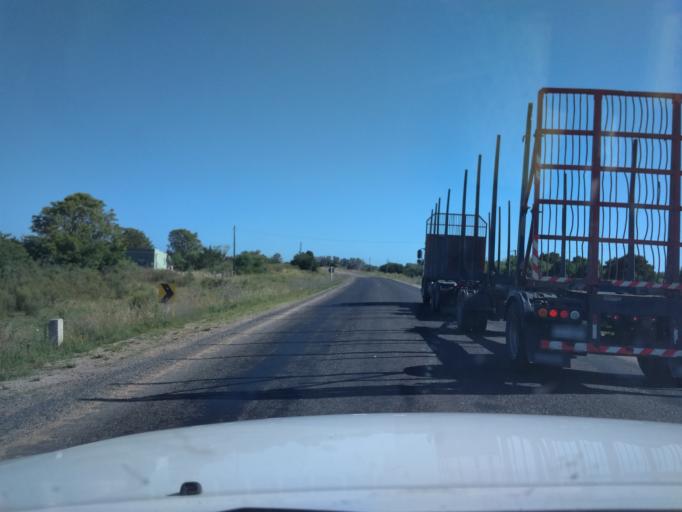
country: UY
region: Canelones
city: San Ramon
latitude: -34.2649
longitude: -55.9282
